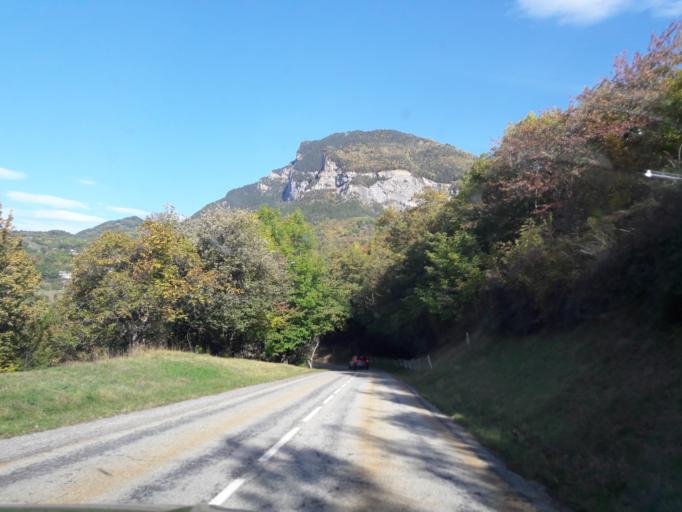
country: FR
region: Rhone-Alpes
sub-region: Departement de la Savoie
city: Saint-Jean-de-Maurienne
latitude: 45.3117
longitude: 6.3532
